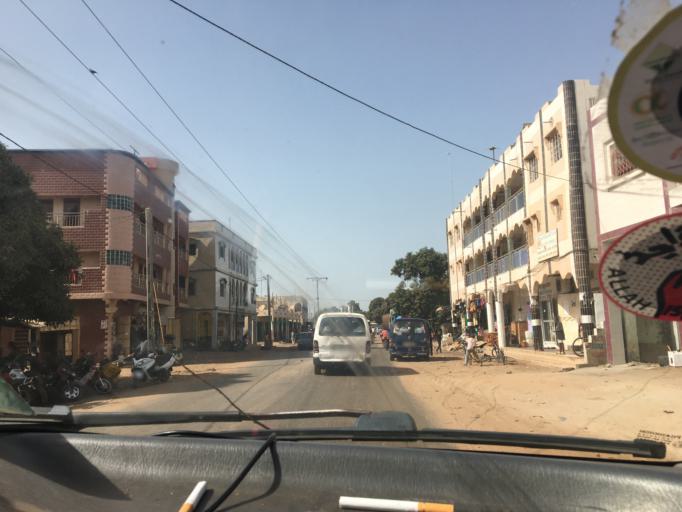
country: GM
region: Western
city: Abuko
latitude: 13.3941
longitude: -16.6740
